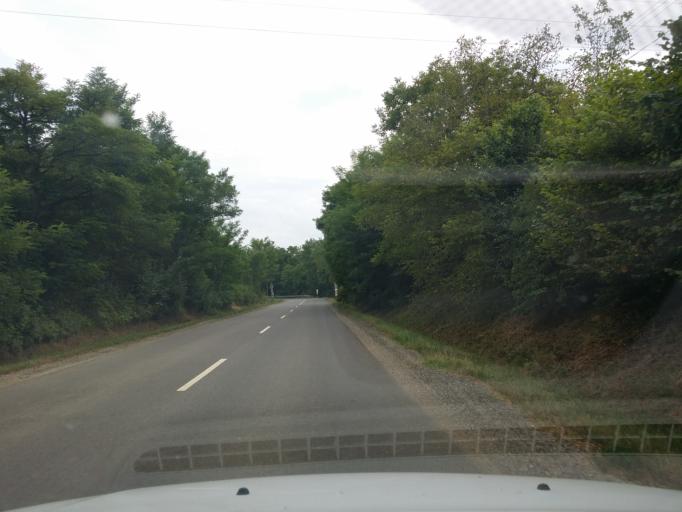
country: HU
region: Nograd
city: Romhany
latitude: 47.9598
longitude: 19.3522
